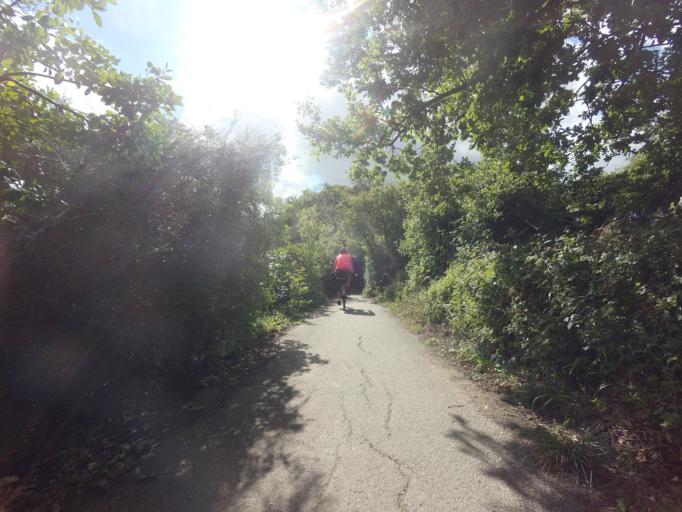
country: GB
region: England
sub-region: East Sussex
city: Hailsham
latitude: 50.8247
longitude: 0.2570
